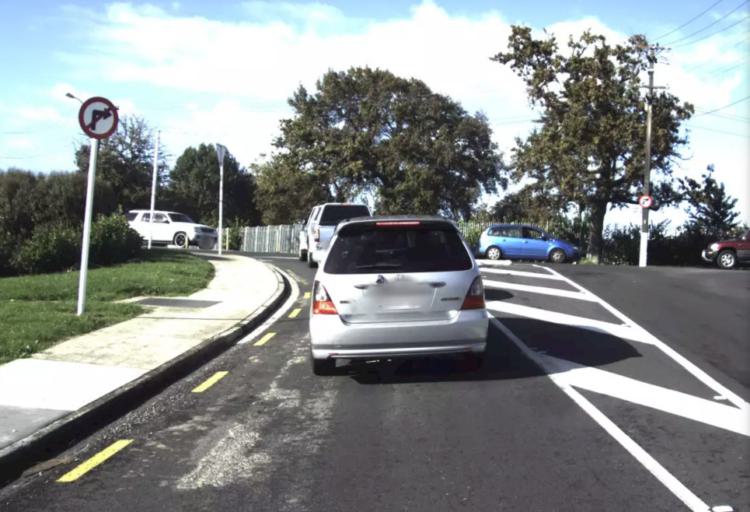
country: NZ
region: Auckland
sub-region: Auckland
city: Papakura
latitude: -37.0621
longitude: 174.9473
